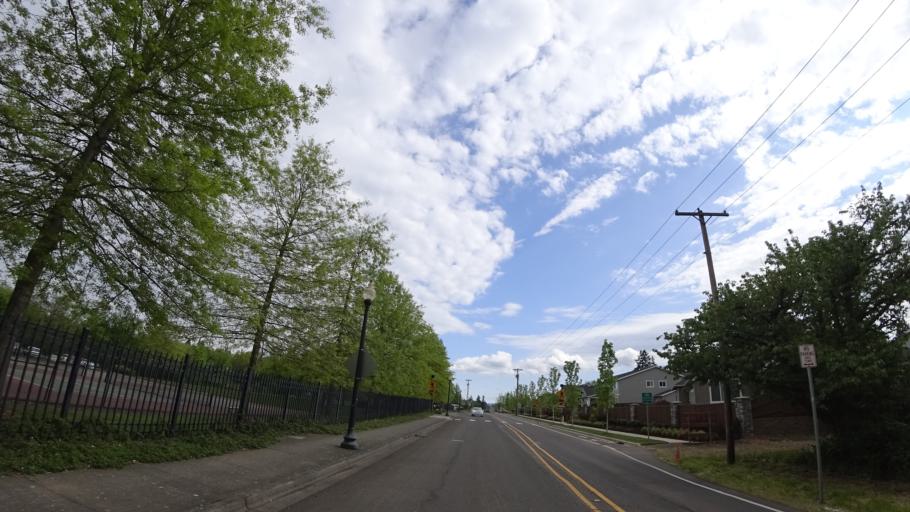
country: US
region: Oregon
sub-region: Washington County
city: Hillsboro
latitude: 45.4924
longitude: -122.9523
